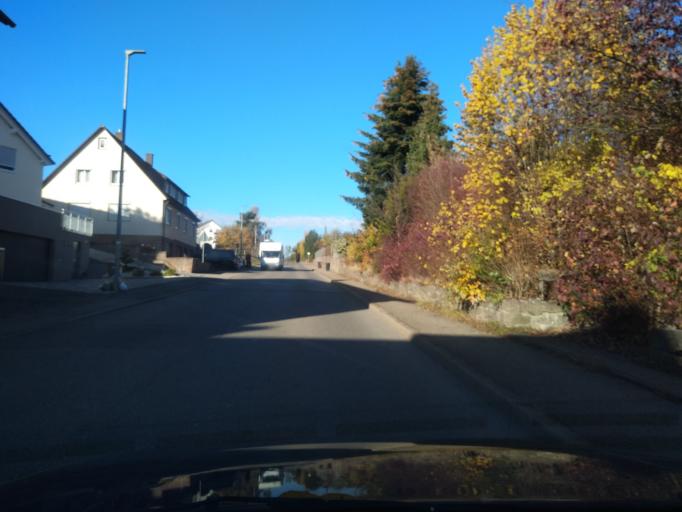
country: DE
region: Baden-Wuerttemberg
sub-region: Karlsruhe Region
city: Bad Liebenzell
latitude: 48.7683
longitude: 8.7548
